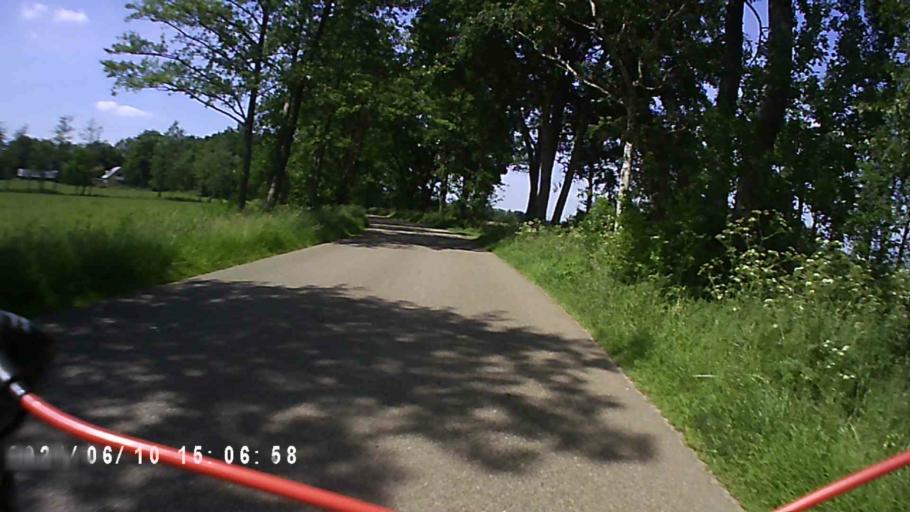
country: NL
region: Friesland
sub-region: Gemeente Achtkarspelen
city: Surhuizum
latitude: 53.1940
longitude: 6.2108
